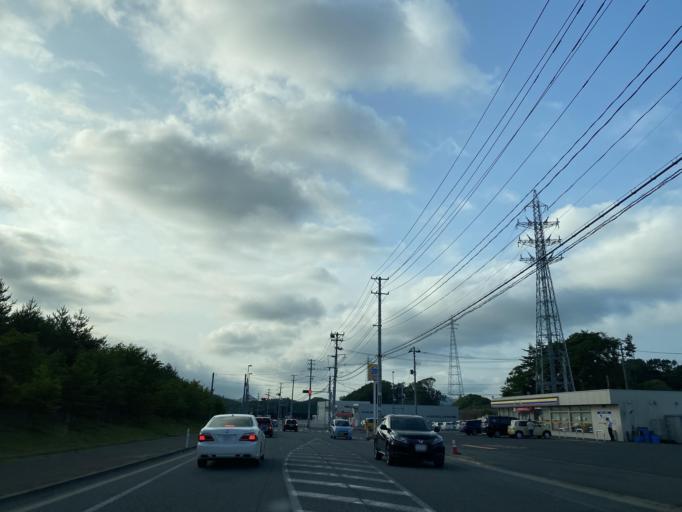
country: JP
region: Miyagi
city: Tomiya
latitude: 38.3659
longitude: 140.8592
